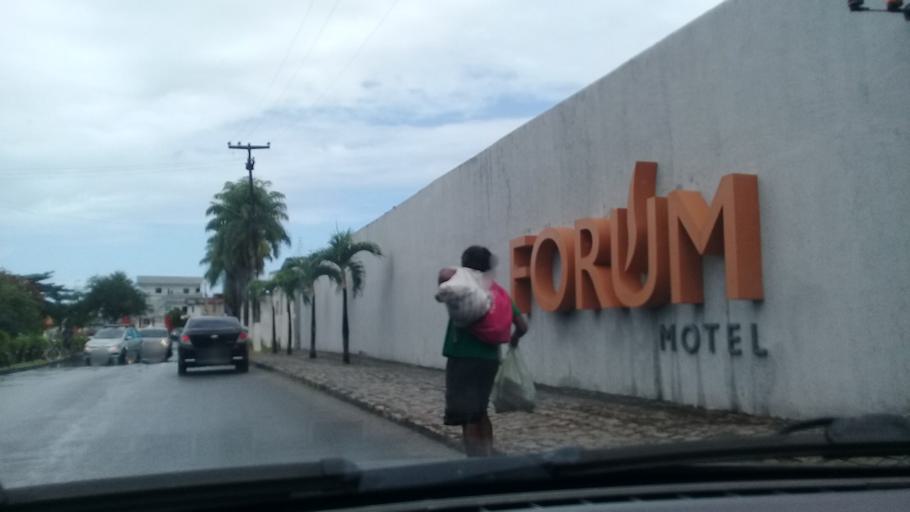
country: BR
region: Pernambuco
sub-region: Jaboatao Dos Guararapes
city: Jaboatao
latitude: -8.1441
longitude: -34.9166
